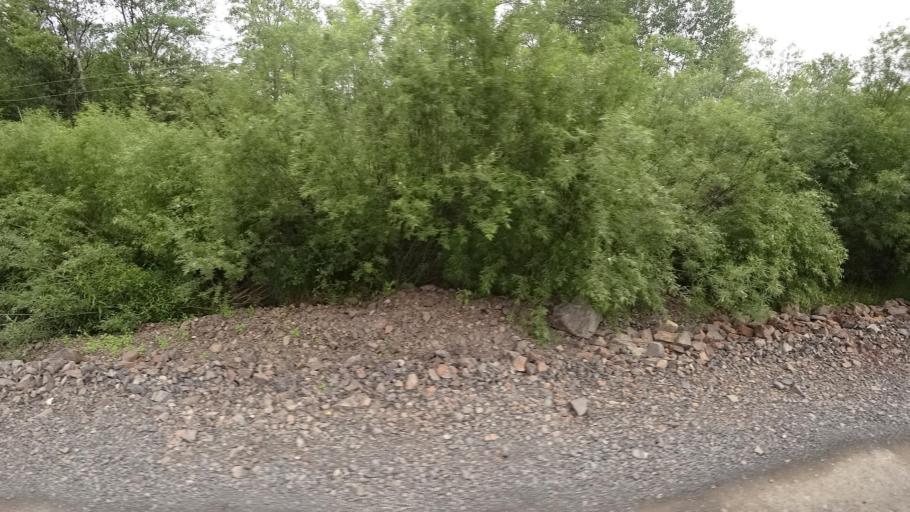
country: RU
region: Khabarovsk Krai
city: Amursk
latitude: 49.8944
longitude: 136.1240
